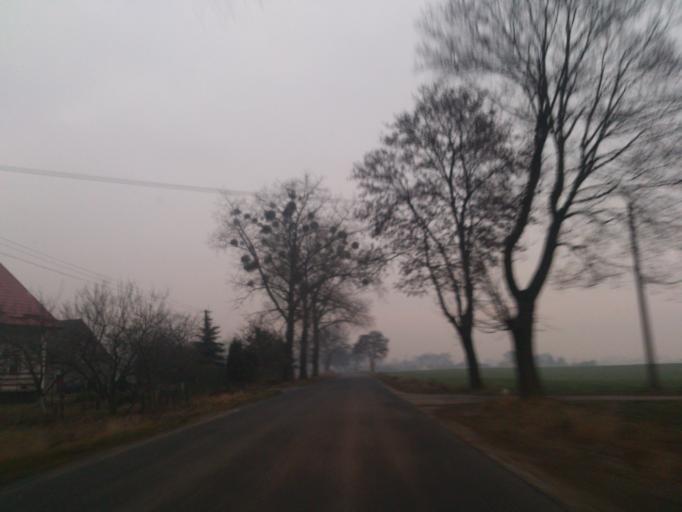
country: PL
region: Kujawsko-Pomorskie
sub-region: Powiat rypinski
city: Wapielsk
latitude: 53.2066
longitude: 19.2118
